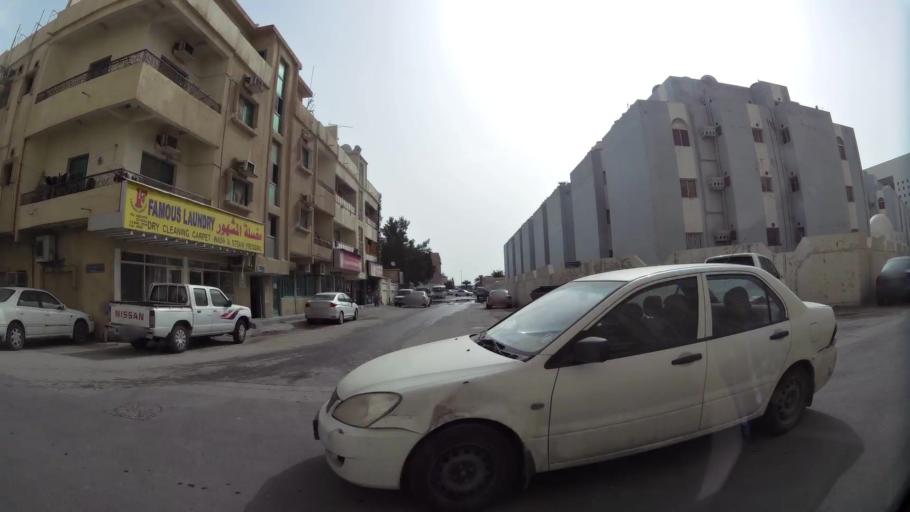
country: QA
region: Baladiyat ad Dawhah
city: Doha
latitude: 25.2766
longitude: 51.5500
